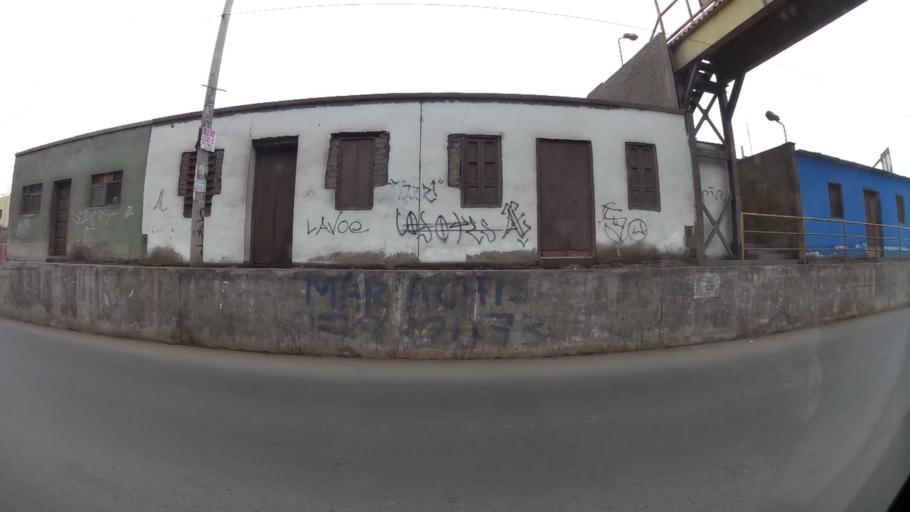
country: PE
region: Lima
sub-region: Lima
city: Punta Hermosa
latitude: -12.2526
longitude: -76.8965
